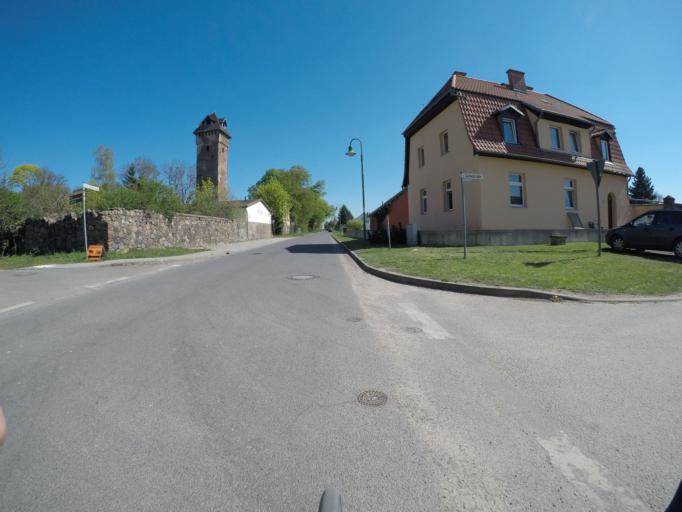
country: DE
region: Brandenburg
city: Werftpfuhl
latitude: 52.6367
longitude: 13.7992
